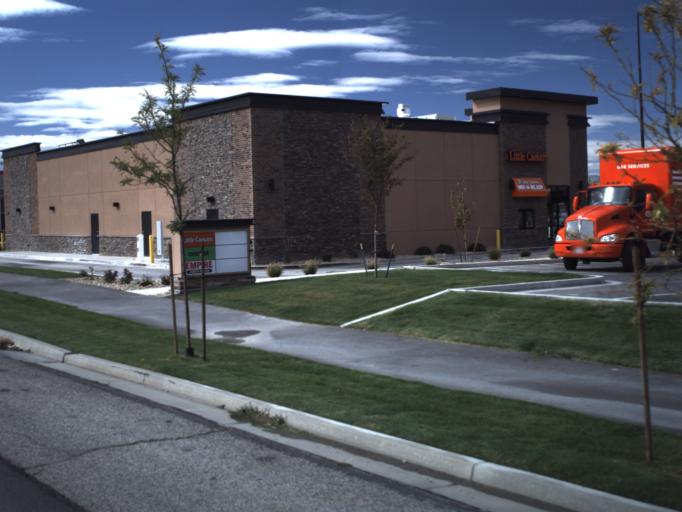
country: US
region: Utah
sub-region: Davis County
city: North Salt Lake
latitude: 40.8540
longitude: -111.9299
